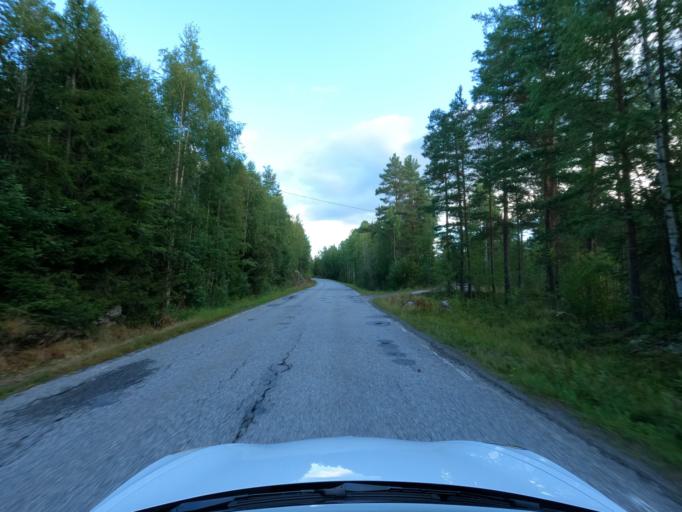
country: NO
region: Telemark
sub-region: Hjartdal
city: Sauland
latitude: 59.8085
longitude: 9.0847
